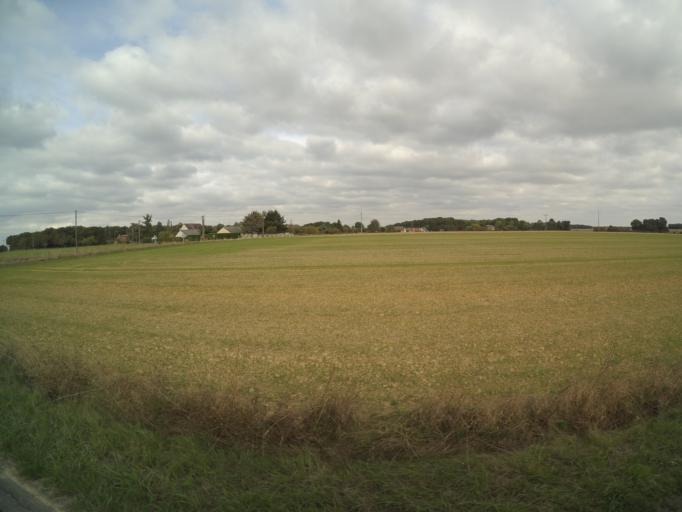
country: FR
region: Centre
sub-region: Departement d'Indre-et-Loire
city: Reugny
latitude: 47.4856
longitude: 0.9365
